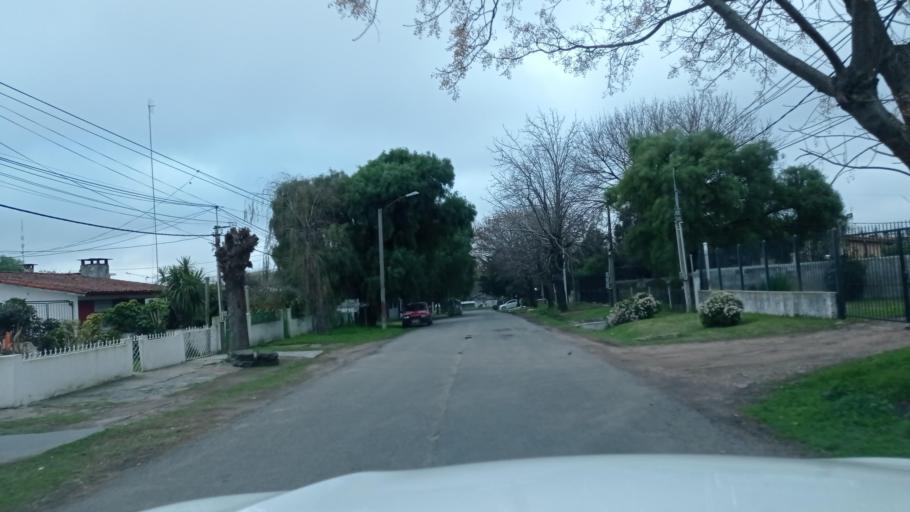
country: UY
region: Canelones
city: La Paz
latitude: -34.8360
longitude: -56.2287
